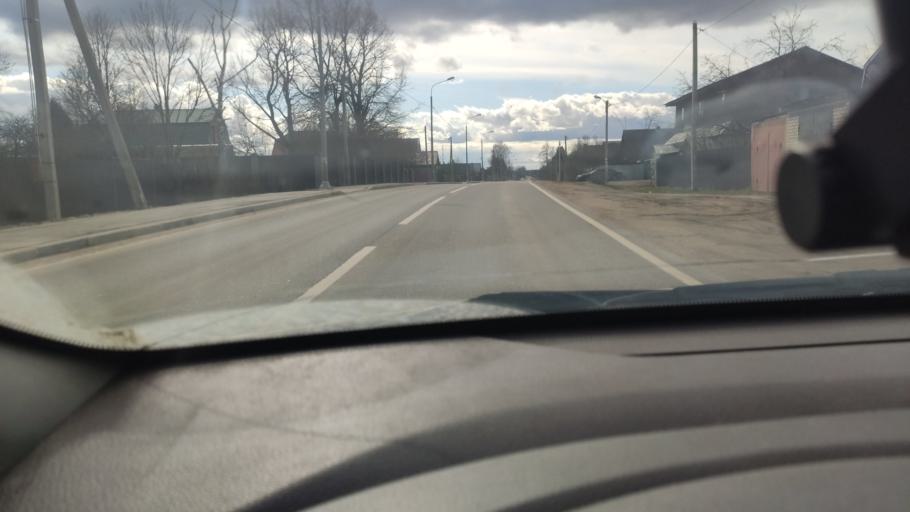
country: RU
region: Moskovskaya
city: Ruza
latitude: 55.7506
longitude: 36.1439
